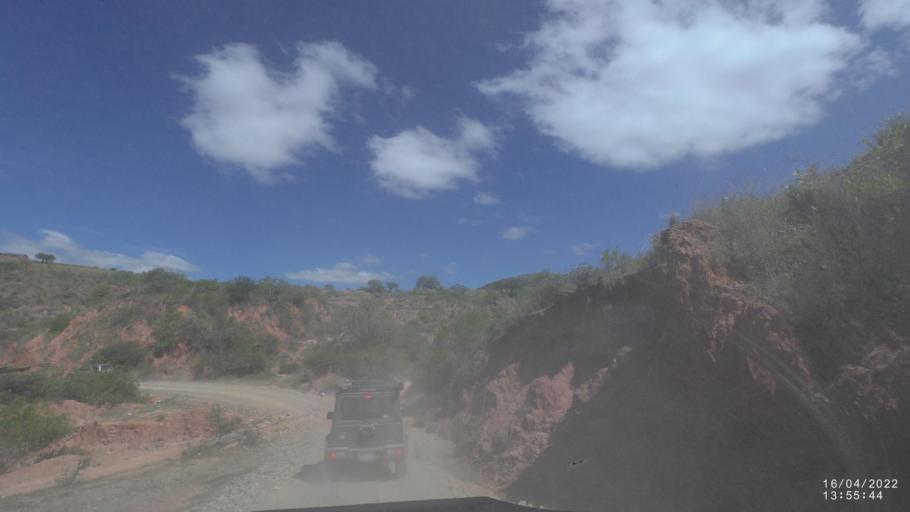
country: BO
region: Cochabamba
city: Mizque
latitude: -18.0303
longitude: -65.5651
